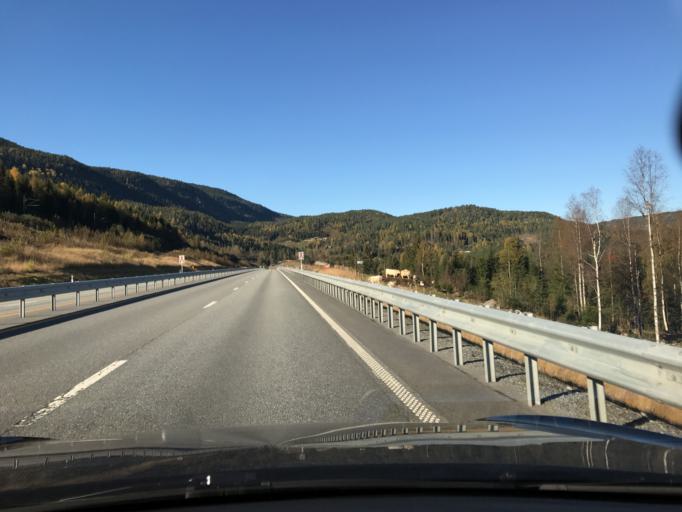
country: NO
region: Buskerud
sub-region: Krodsherad
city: Noresund
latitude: 60.2816
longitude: 9.7588
